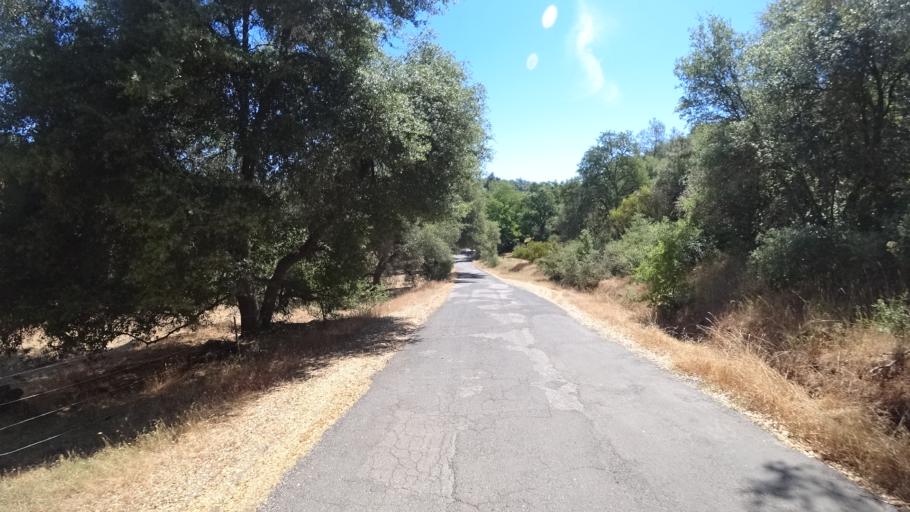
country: US
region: California
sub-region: Calaveras County
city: Angels Camp
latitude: 38.1256
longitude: -120.5754
